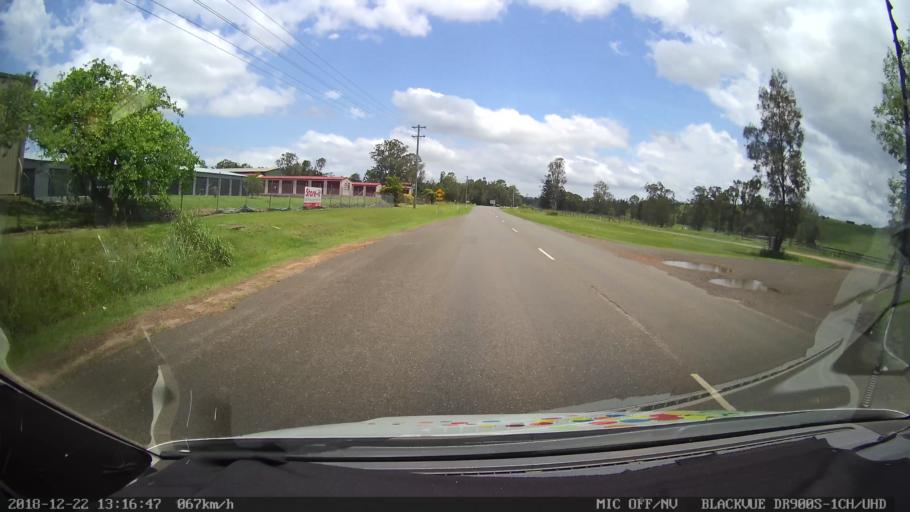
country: AU
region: New South Wales
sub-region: Clarence Valley
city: South Grafton
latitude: -29.7296
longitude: 152.9398
